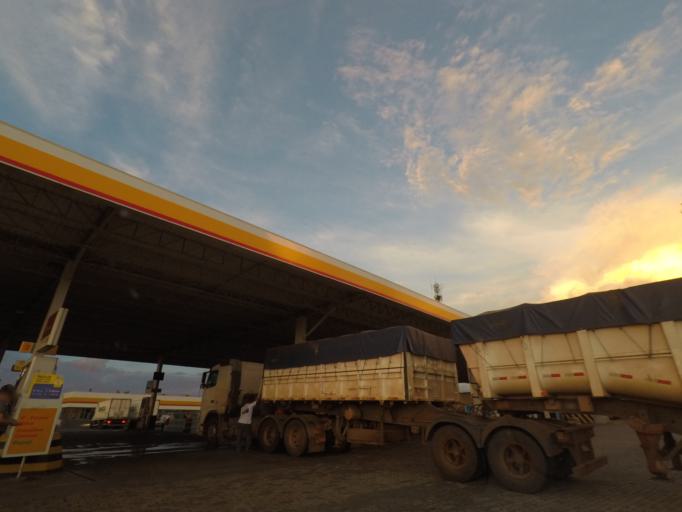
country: BR
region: Minas Gerais
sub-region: Uberaba
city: Uberaba
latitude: -19.5842
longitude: -48.0305
